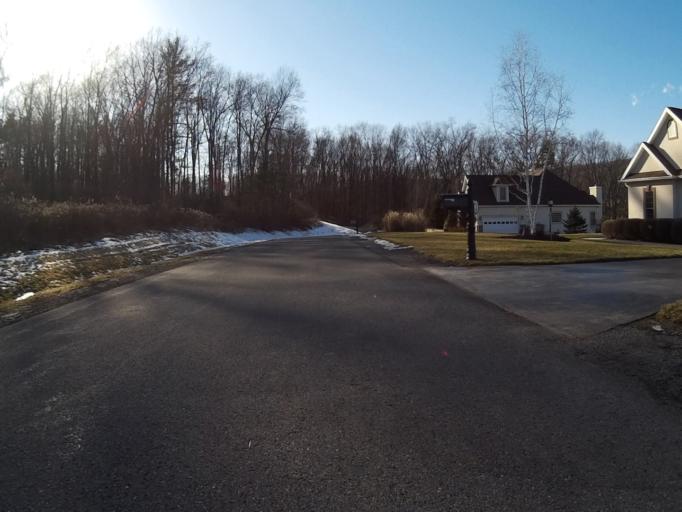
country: US
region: Pennsylvania
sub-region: Centre County
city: Park Forest Village
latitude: 40.8507
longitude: -77.8879
